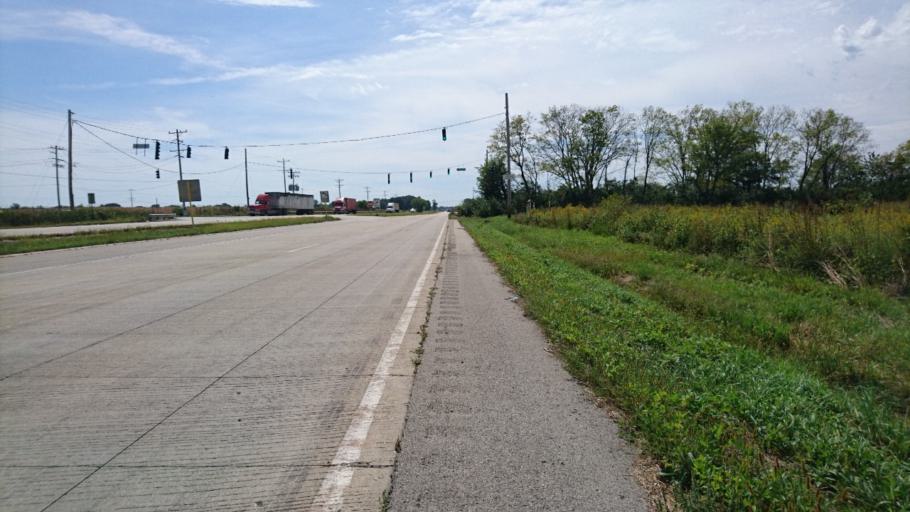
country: US
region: Illinois
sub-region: Will County
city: Wilmington
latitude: 41.3355
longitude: -88.1332
